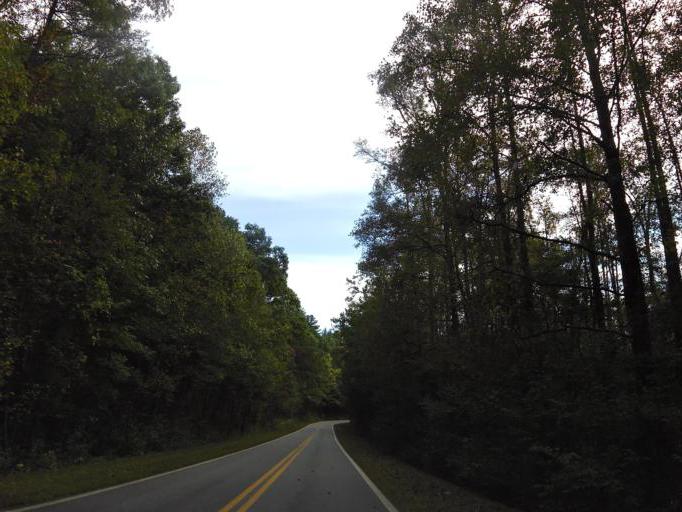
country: US
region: Georgia
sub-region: Pickens County
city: Nelson
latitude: 34.5056
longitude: -84.2765
